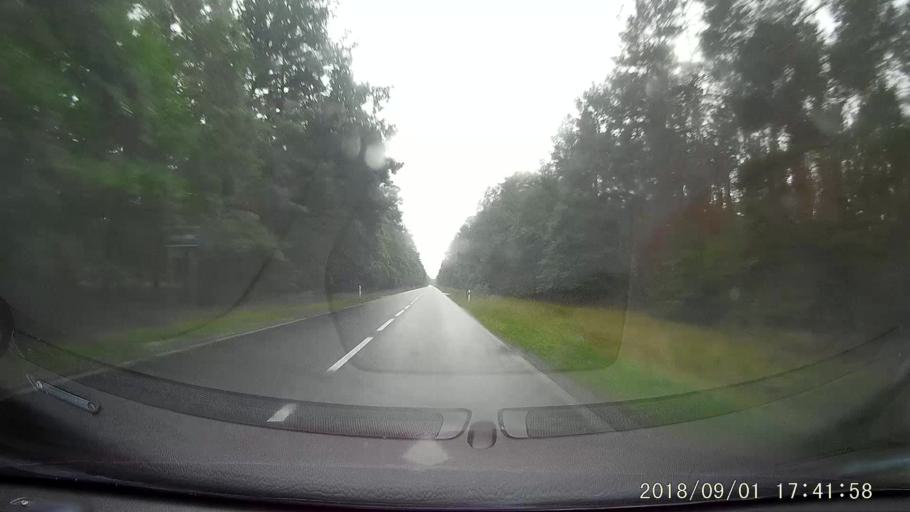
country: PL
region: Lubusz
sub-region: Powiat zaganski
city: Zagan
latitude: 51.5622
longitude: 15.2631
